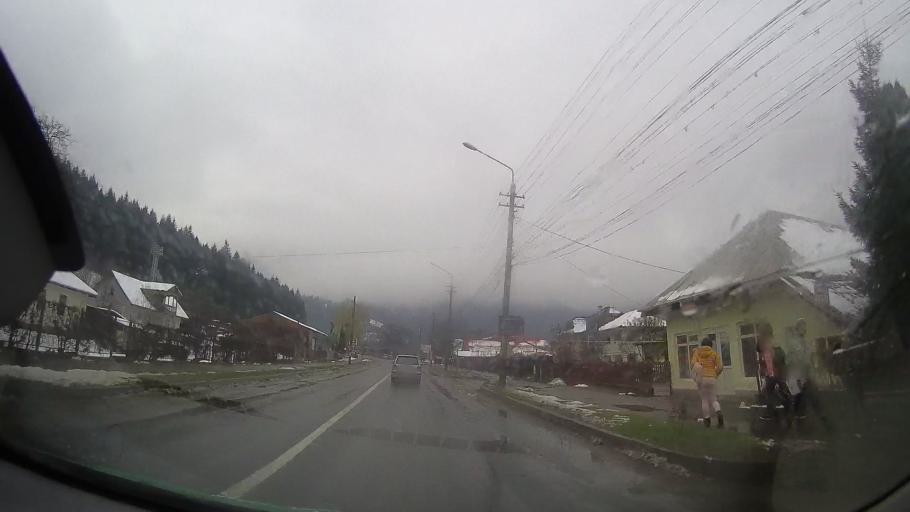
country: RO
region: Neamt
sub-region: Comuna Bicaz
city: Dodeni
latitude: 46.9095
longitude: 26.0982
